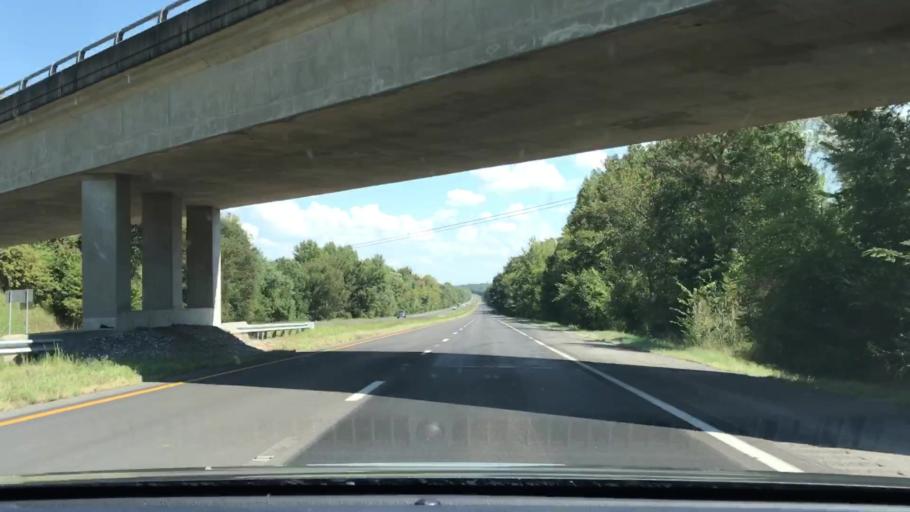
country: US
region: Kentucky
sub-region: Fulton County
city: Fulton
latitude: 36.5885
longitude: -88.8168
